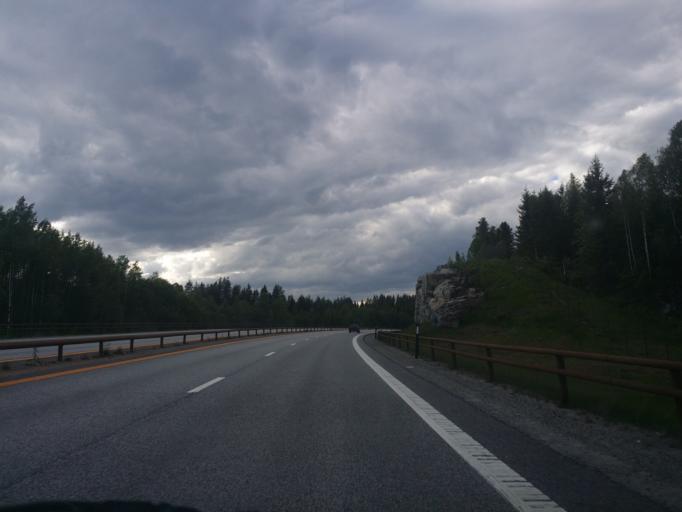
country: NO
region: Akershus
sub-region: Eidsvoll
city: Raholt
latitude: 60.2705
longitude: 11.1573
